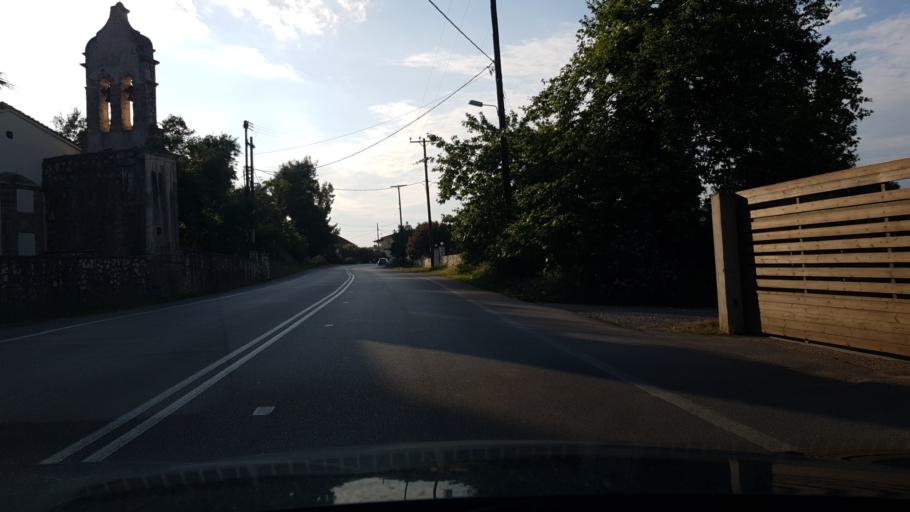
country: GR
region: Ionian Islands
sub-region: Lefkada
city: Lefkada
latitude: 38.8156
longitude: 20.7048
